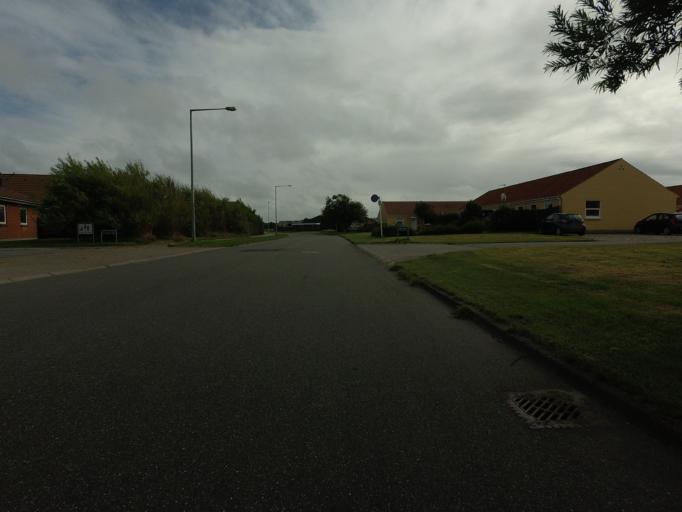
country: DK
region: North Denmark
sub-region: Jammerbugt Kommune
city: Pandrup
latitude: 57.3649
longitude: 9.7164
